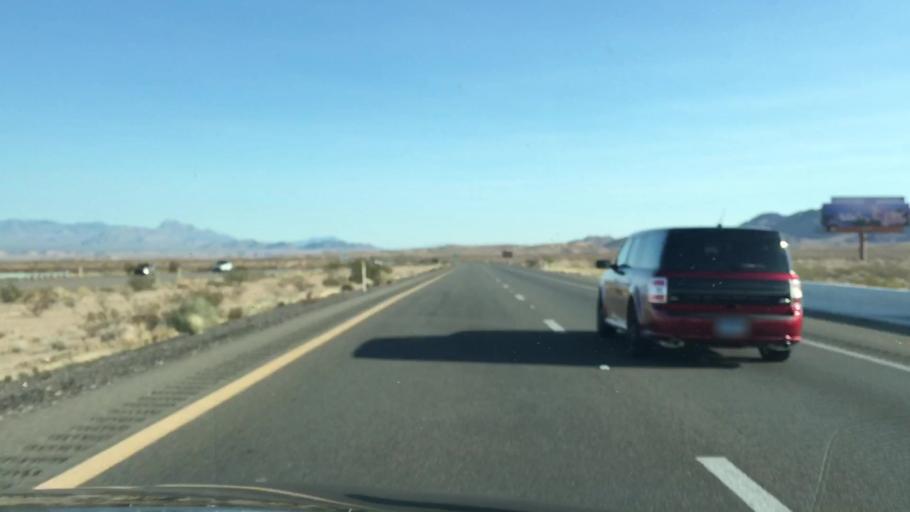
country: US
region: Nevada
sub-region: Clark County
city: Moapa Town
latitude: 36.5774
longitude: -114.6602
